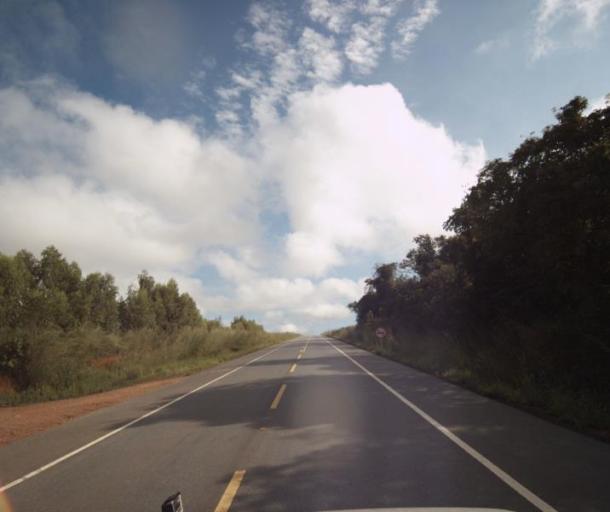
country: BR
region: Goias
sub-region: Barro Alto
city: Barro Alto
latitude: -15.2597
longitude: -48.6871
